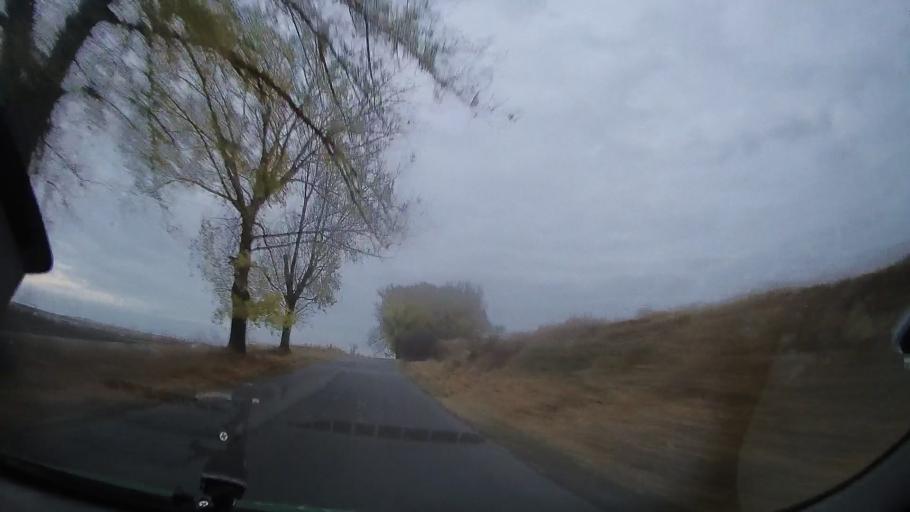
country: RO
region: Tulcea
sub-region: Comuna Mihai Bravu
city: Turda
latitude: 44.9661
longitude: 28.6334
